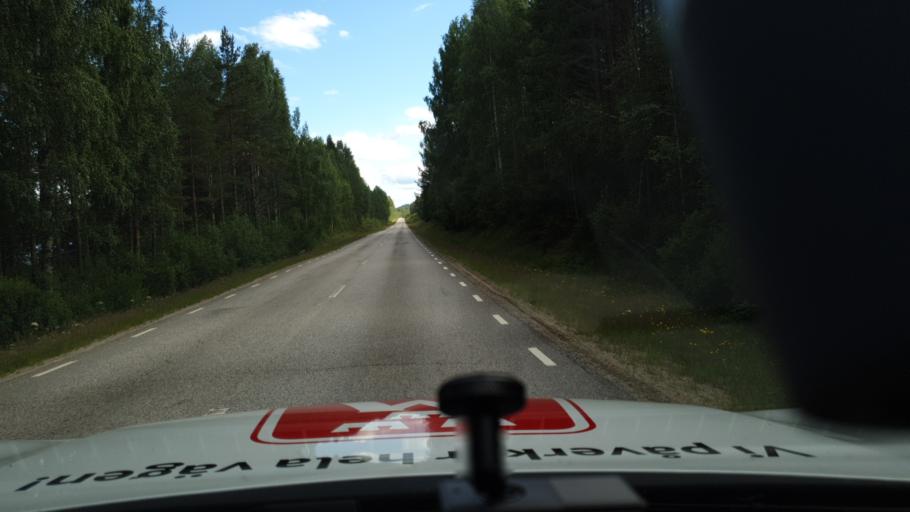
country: NO
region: Hedmark
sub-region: Trysil
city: Innbygda
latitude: 61.0203
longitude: 12.4701
